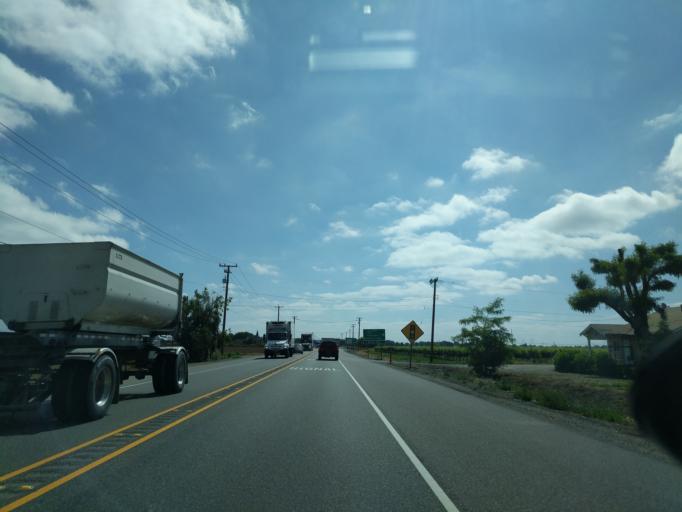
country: US
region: California
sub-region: Contra Costa County
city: Byron
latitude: 37.8965
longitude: -121.6468
